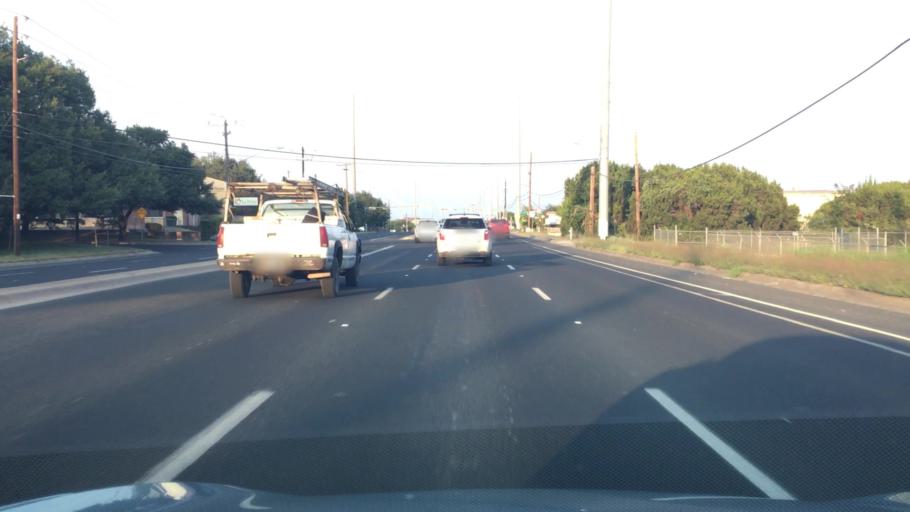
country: US
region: Texas
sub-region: Travis County
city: Manchaca
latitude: 30.1738
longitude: -97.8116
